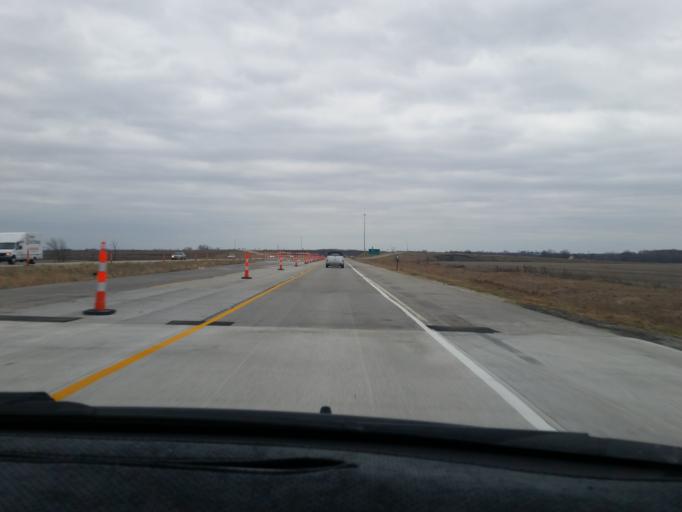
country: US
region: Kansas
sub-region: Douglas County
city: Eudora
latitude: 38.9352
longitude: -95.1581
